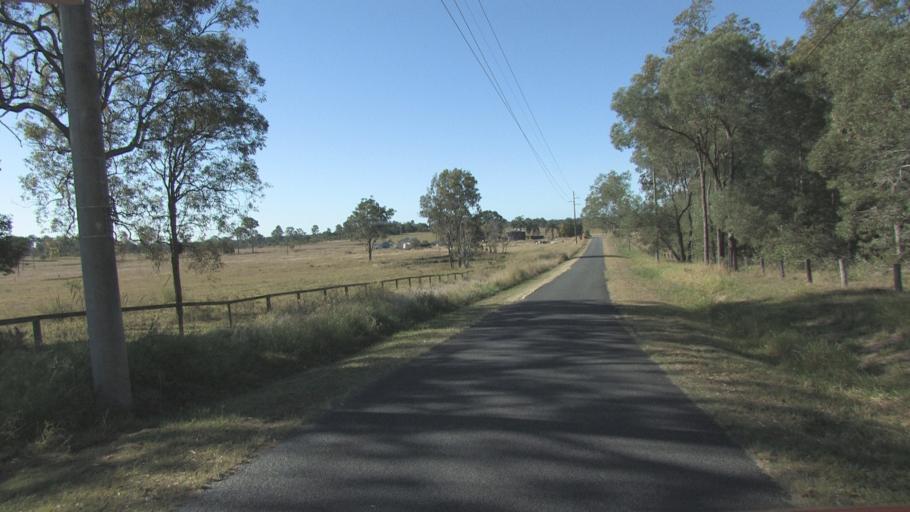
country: AU
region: Queensland
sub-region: Logan
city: Chambers Flat
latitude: -27.7684
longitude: 153.0604
